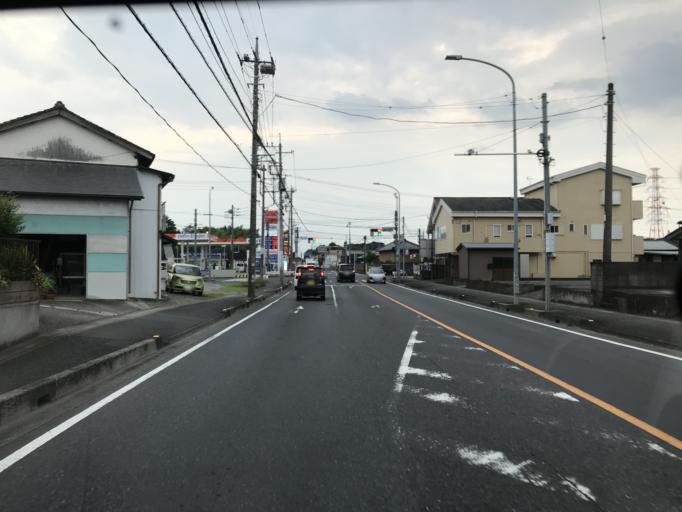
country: JP
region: Saitama
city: Sugito
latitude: 36.0073
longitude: 139.6977
